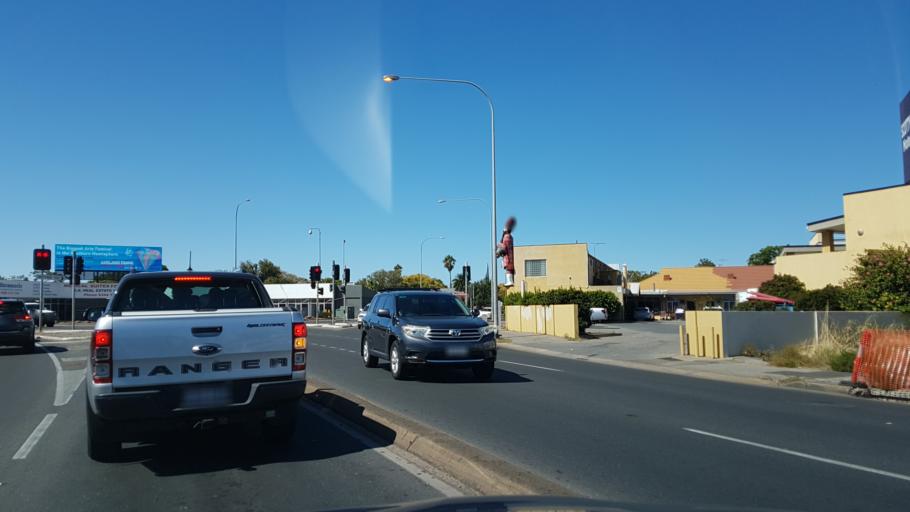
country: AU
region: South Australia
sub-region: Prospect
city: Prospect
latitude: -34.8939
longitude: 138.6031
